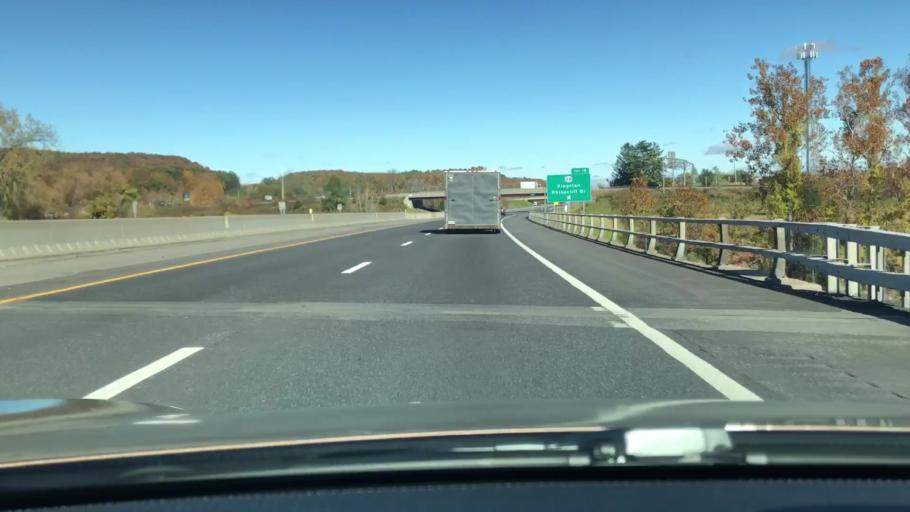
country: US
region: New York
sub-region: Ulster County
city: Hurley
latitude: 41.9436
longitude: -74.0323
